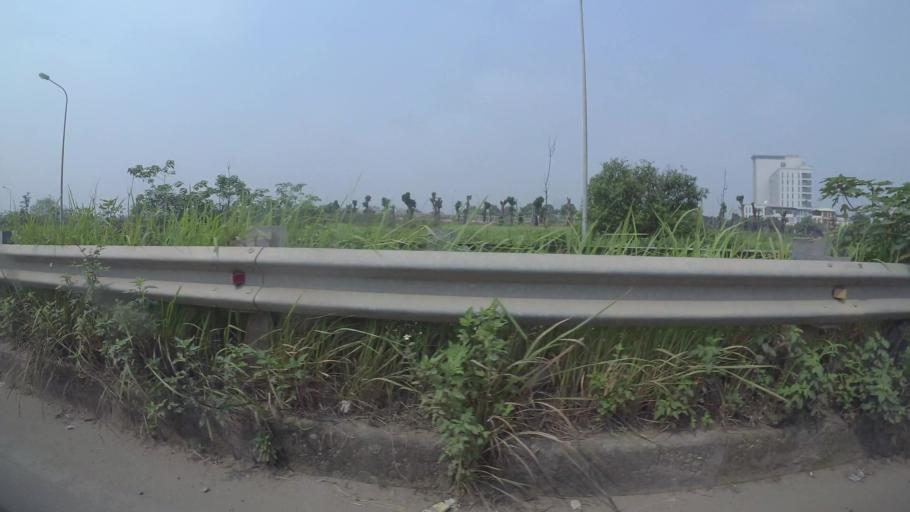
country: VN
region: Ha Noi
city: Cau Dien
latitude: 21.0118
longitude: 105.7484
